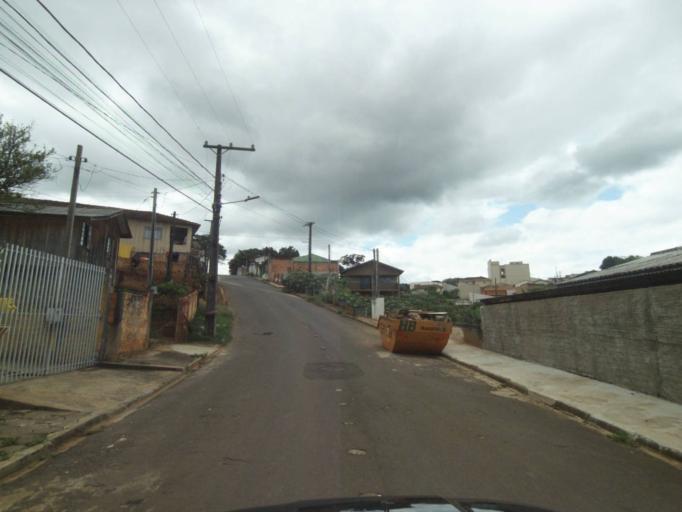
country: BR
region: Parana
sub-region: Telemaco Borba
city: Telemaco Borba
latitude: -24.3245
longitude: -50.6359
